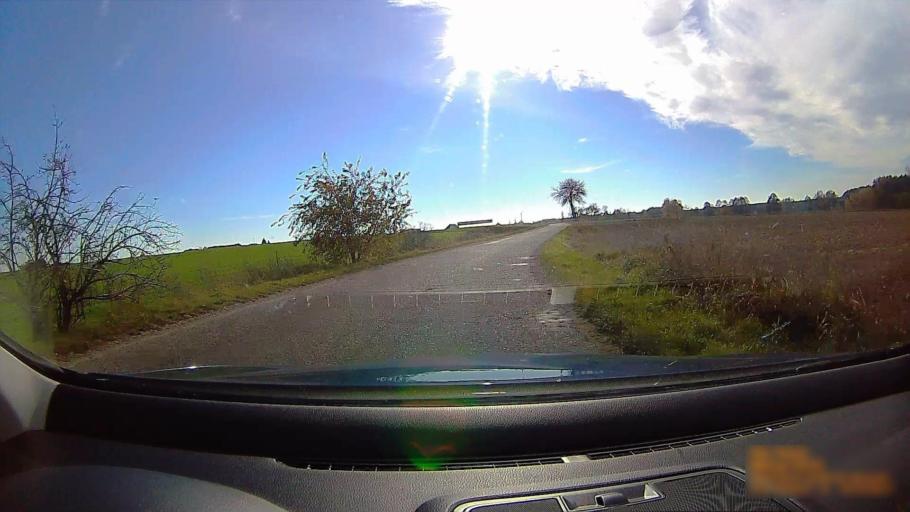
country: PL
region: Greater Poland Voivodeship
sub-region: Powiat ostrzeszowski
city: Doruchow
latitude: 51.3990
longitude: 18.0301
